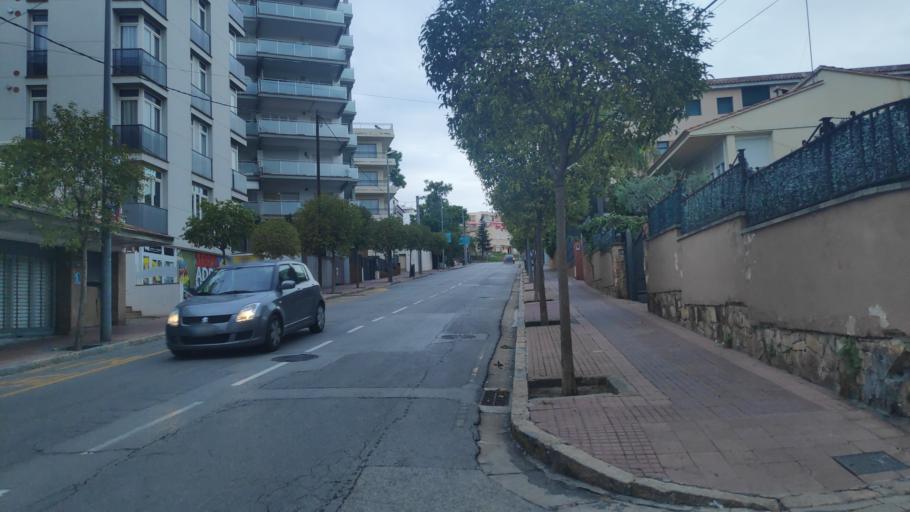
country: ES
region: Catalonia
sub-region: Provincia de Girona
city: Lloret de Mar
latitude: 41.7027
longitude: 2.8552
